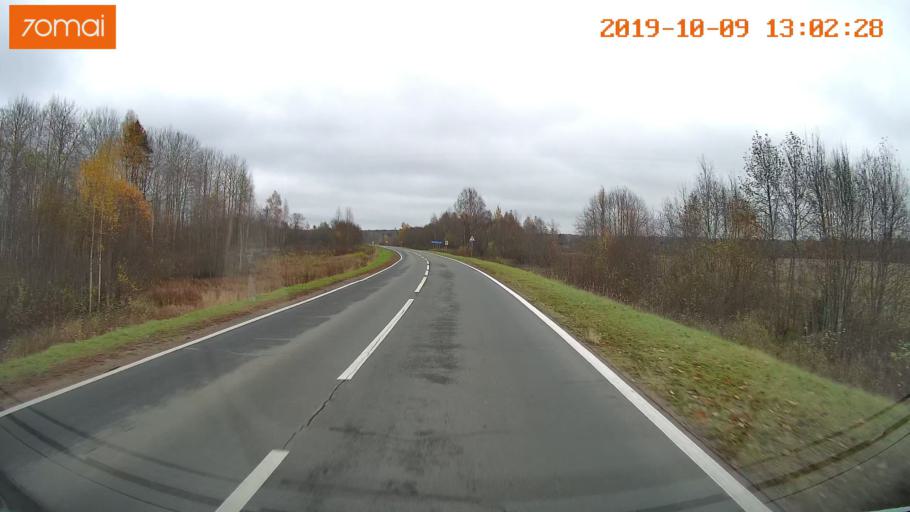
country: RU
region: Jaroslavl
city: Prechistoye
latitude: 58.3612
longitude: 40.5021
